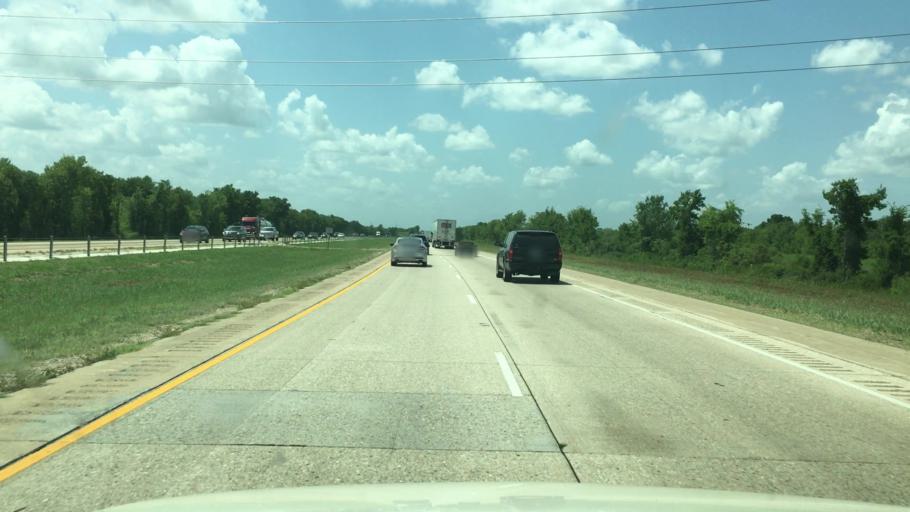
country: US
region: Arkansas
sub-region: Miller County
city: Texarkana
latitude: 33.5833
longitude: -93.8420
